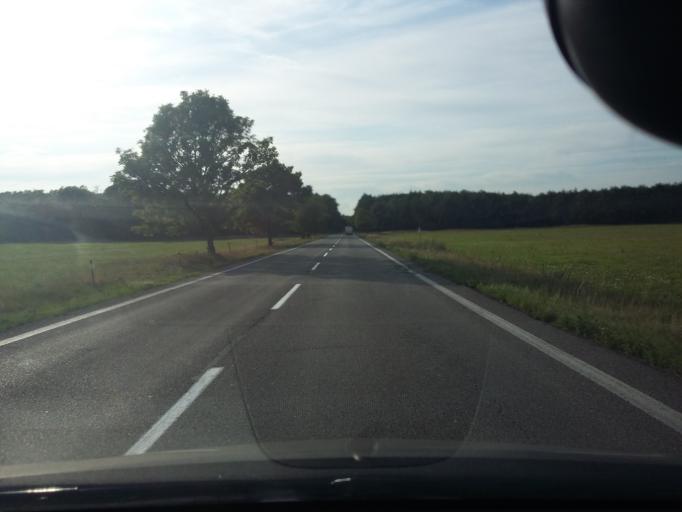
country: SK
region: Bratislavsky
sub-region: Okres Malacky
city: Malacky
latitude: 48.3862
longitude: 17.1051
